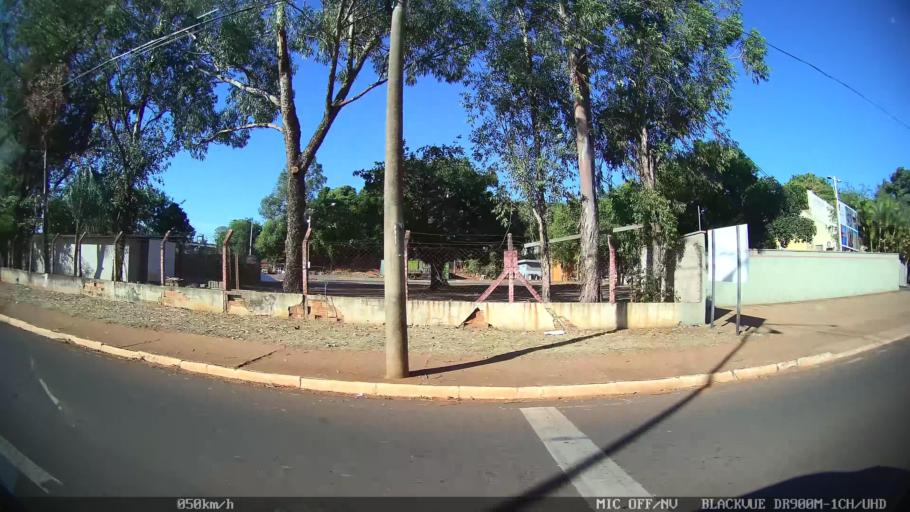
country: BR
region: Sao Paulo
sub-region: Olimpia
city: Olimpia
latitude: -20.7217
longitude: -48.9060
